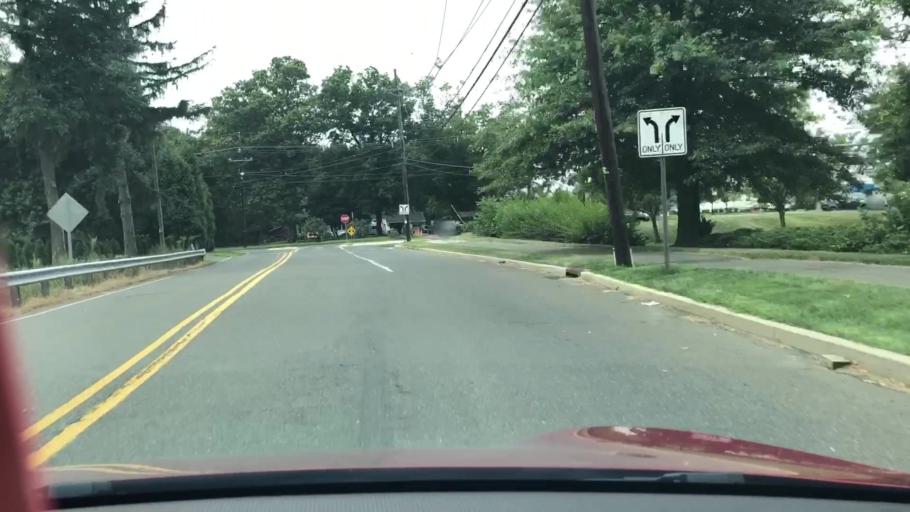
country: US
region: New Jersey
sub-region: Mercer County
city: Yardville
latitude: 40.1895
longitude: -74.6435
